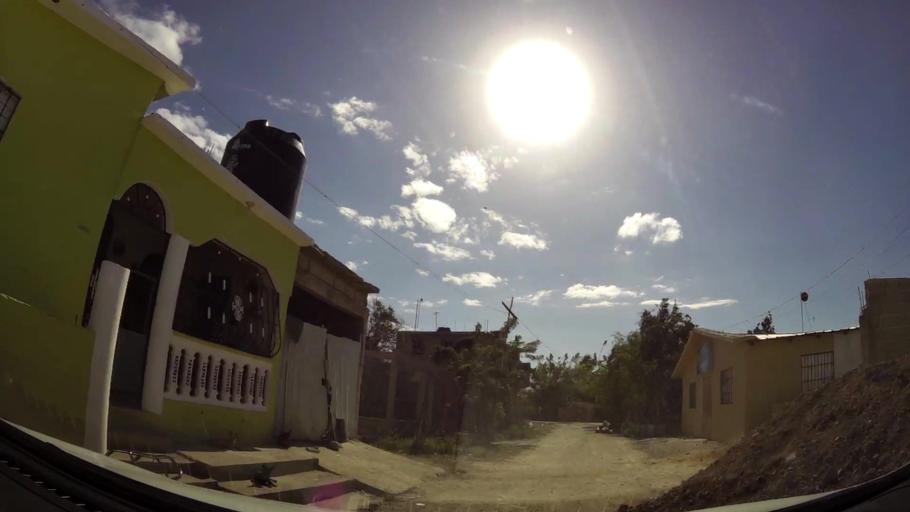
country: DO
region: Santo Domingo
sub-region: Santo Domingo
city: Boca Chica
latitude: 18.4638
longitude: -69.6016
